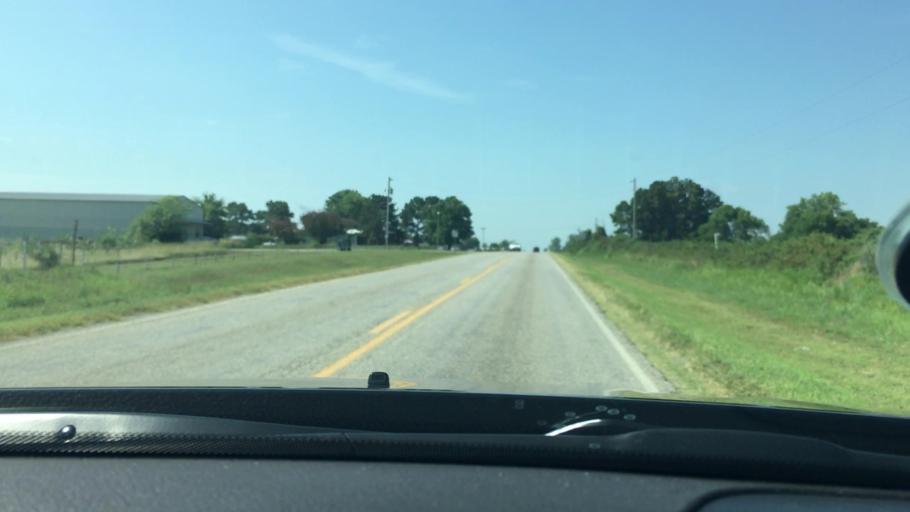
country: US
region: Oklahoma
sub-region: Johnston County
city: Tishomingo
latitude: 34.2801
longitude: -96.4248
